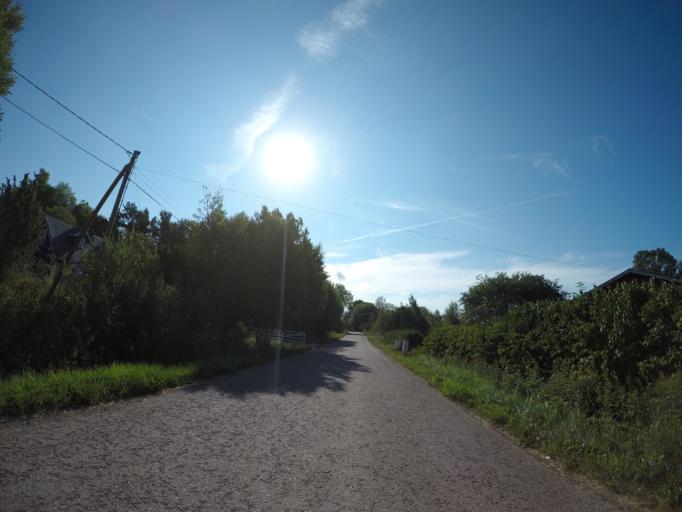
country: AX
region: Alands landsbygd
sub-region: Finstroem
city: Finstroem
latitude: 60.2509
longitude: 19.9164
